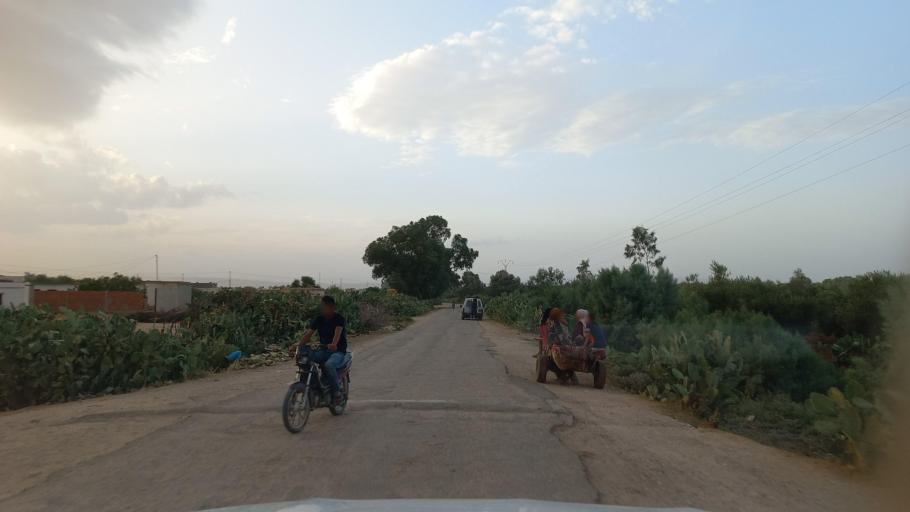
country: TN
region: Al Qasrayn
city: Kasserine
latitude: 35.2663
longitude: 9.0601
